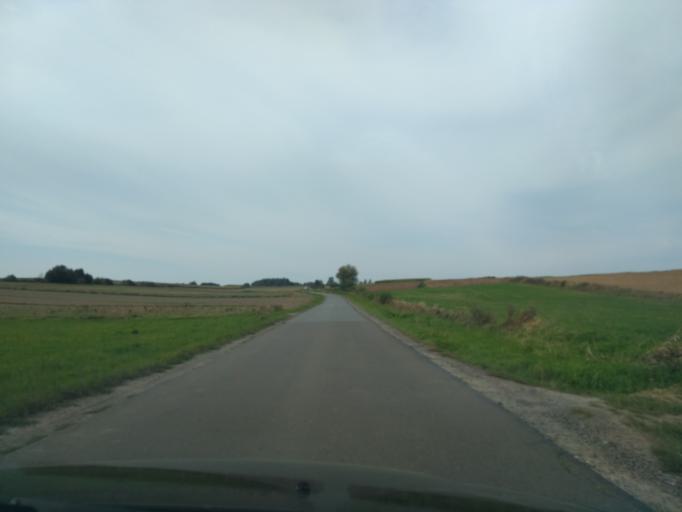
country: PL
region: Subcarpathian Voivodeship
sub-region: Powiat rzeszowski
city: Zglobien
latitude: 50.0190
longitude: 21.8477
